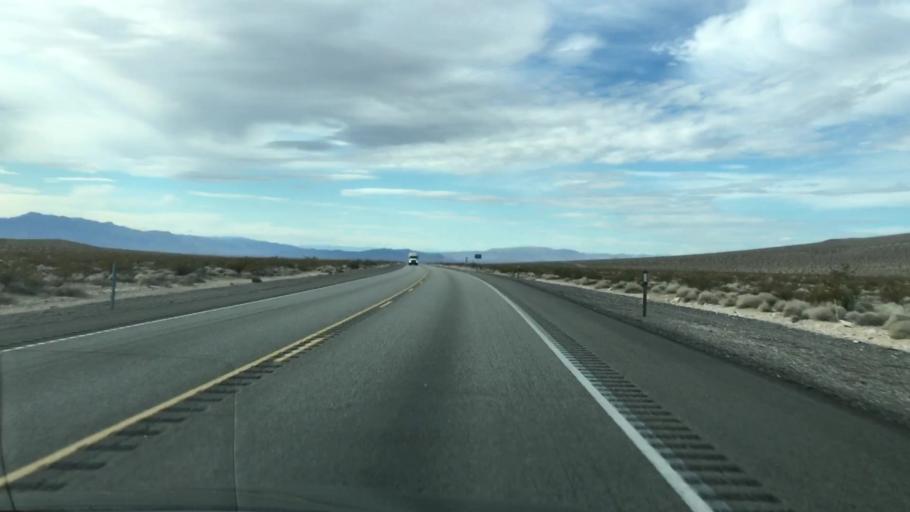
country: US
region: Nevada
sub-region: Nye County
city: Beatty
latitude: 36.6316
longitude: -116.3224
